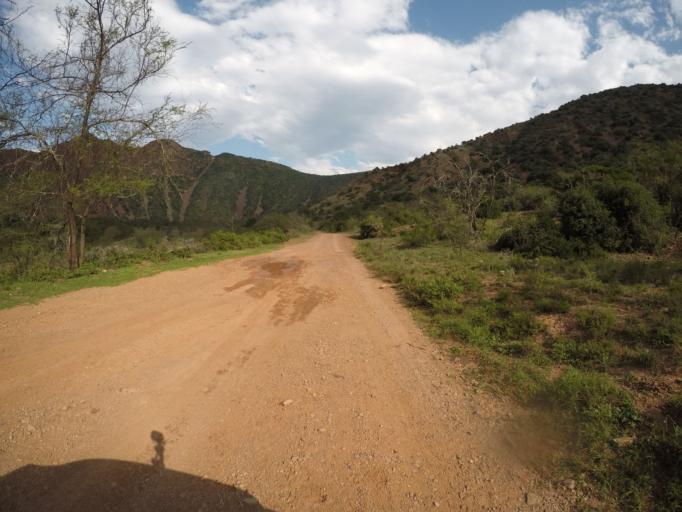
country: ZA
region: Eastern Cape
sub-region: Cacadu District Municipality
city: Kareedouw
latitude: -33.6376
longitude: 24.3165
